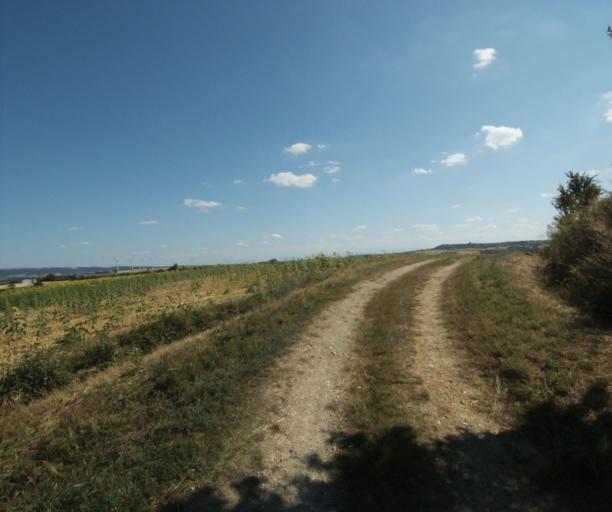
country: FR
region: Midi-Pyrenees
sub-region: Departement de la Haute-Garonne
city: Saint-Felix-Lauragais
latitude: 43.4853
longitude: 1.9046
